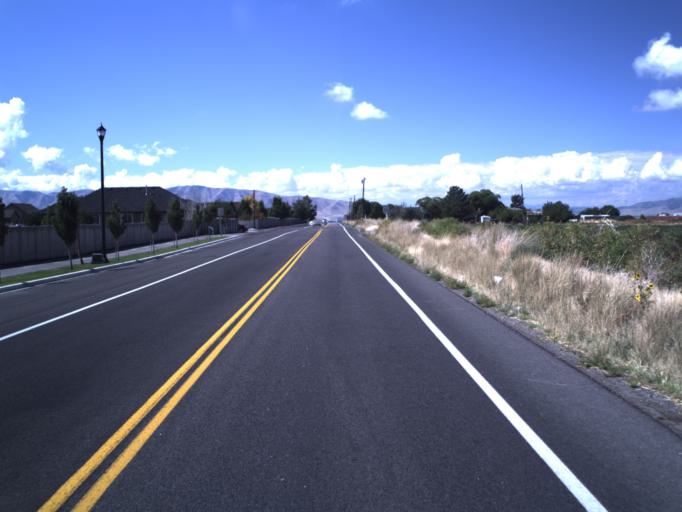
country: US
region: Utah
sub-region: Utah County
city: Spanish Fork
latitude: 40.1154
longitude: -111.6242
